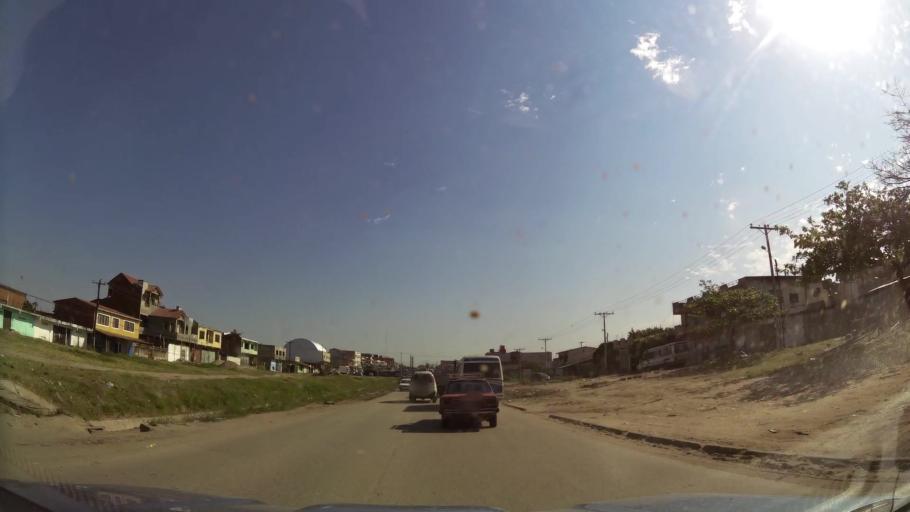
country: BO
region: Santa Cruz
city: Santa Cruz de la Sierra
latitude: -17.8232
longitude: -63.1287
